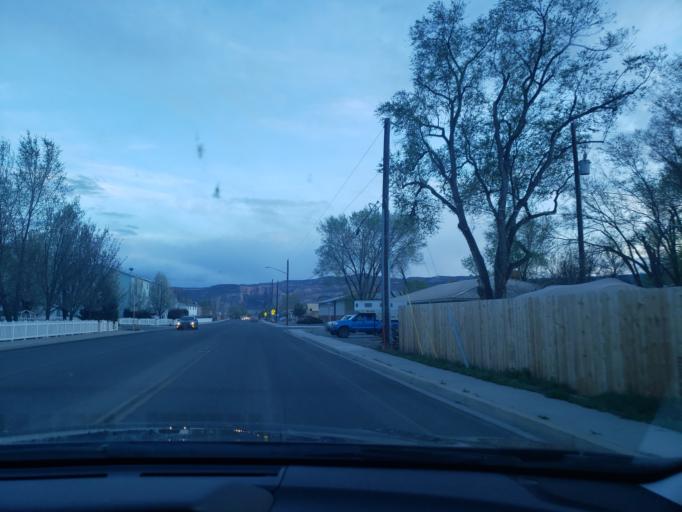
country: US
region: Colorado
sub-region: Mesa County
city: Fruita
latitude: 39.1586
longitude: -108.7198
